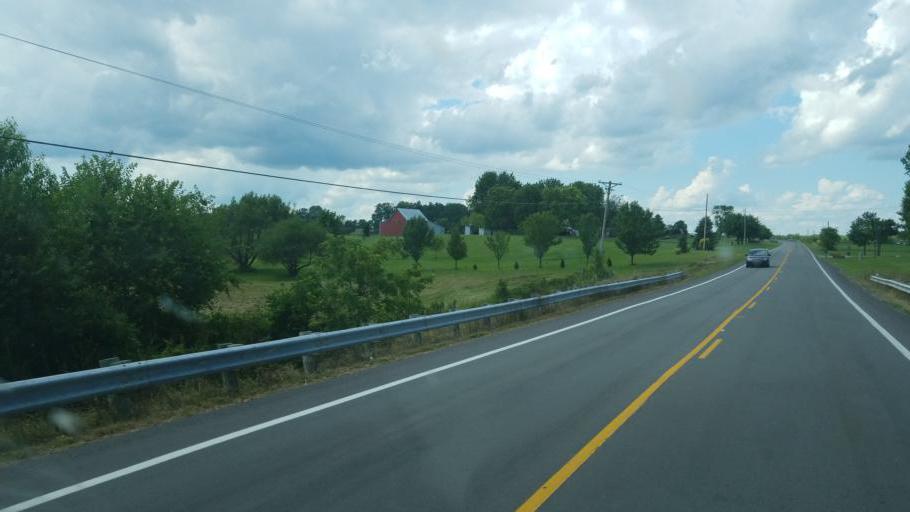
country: US
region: Ohio
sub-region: Highland County
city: Greenfield
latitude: 39.3718
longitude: -83.3791
